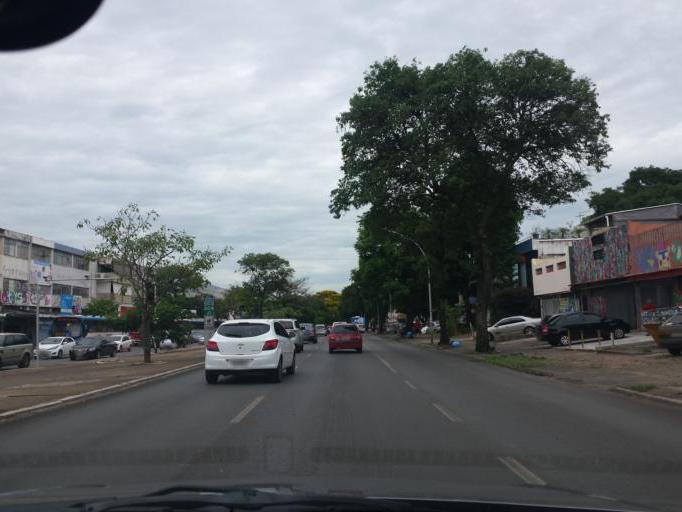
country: BR
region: Federal District
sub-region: Brasilia
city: Brasilia
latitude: -15.8062
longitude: -47.8990
